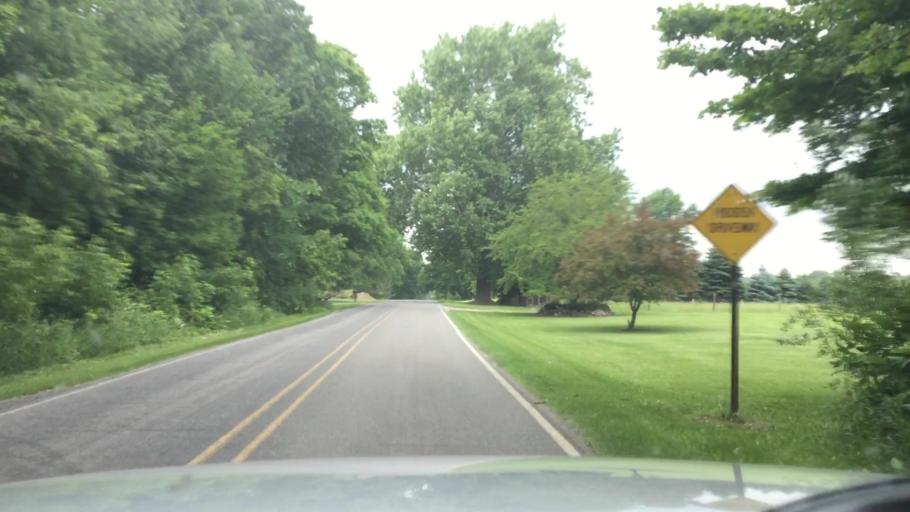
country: US
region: Michigan
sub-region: Shiawassee County
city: Durand
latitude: 42.7864
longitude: -84.0017
